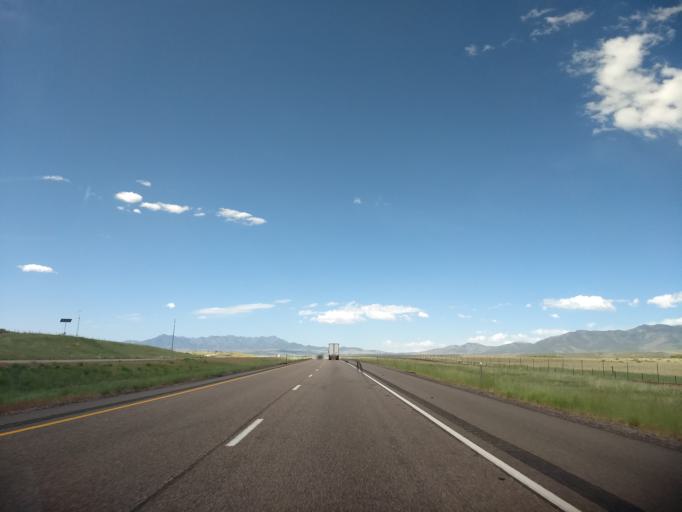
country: US
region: Utah
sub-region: Millard County
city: Fillmore
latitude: 39.0188
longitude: -112.3046
